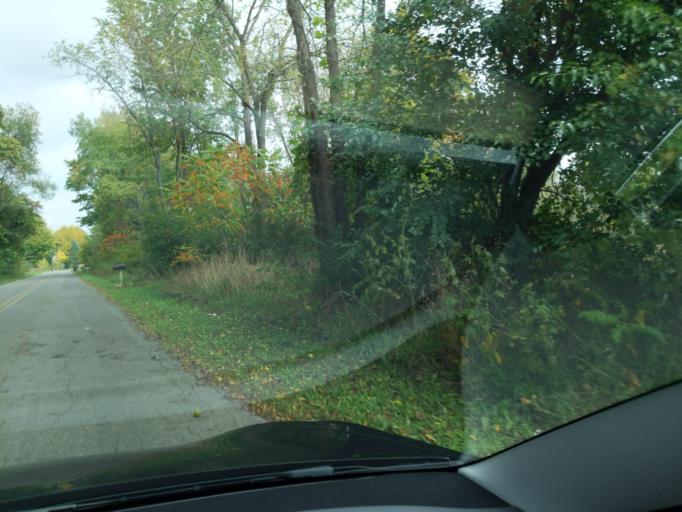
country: US
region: Michigan
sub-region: Ingham County
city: Leslie
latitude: 42.4063
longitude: -84.4860
